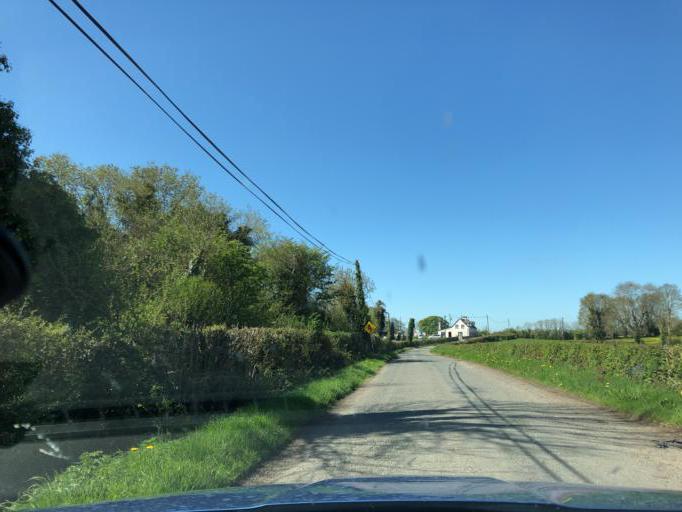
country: IE
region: Connaught
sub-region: County Galway
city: Portumna
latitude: 53.1837
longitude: -8.1694
